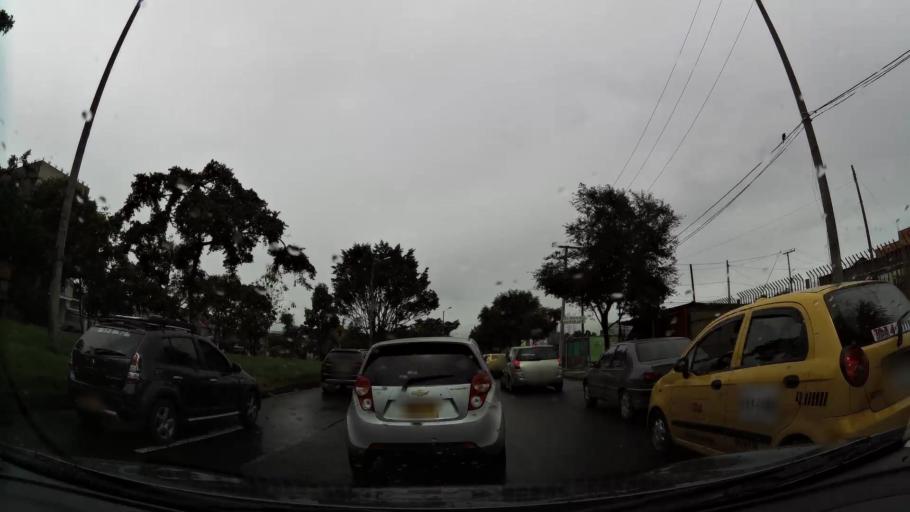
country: CO
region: Bogota D.C.
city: Bogota
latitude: 4.6654
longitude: -74.1067
